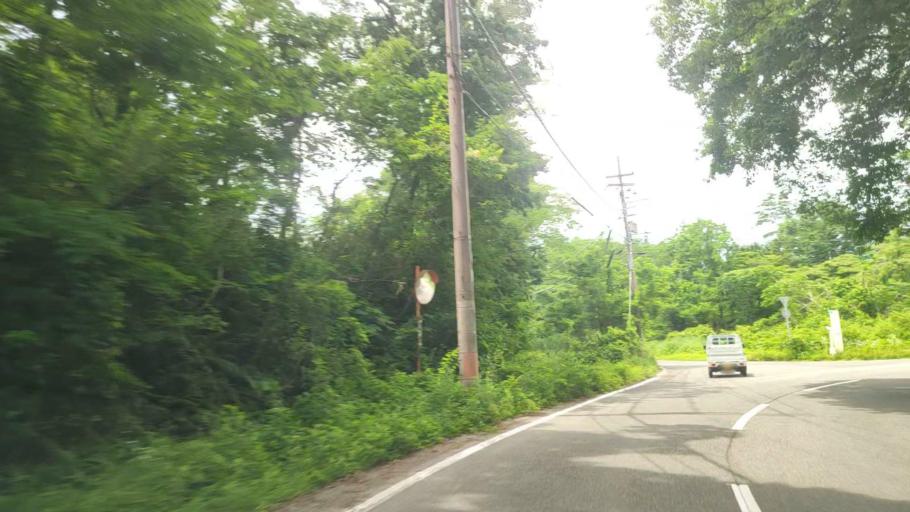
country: JP
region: Hyogo
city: Toyooka
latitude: 35.4971
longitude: 134.6852
